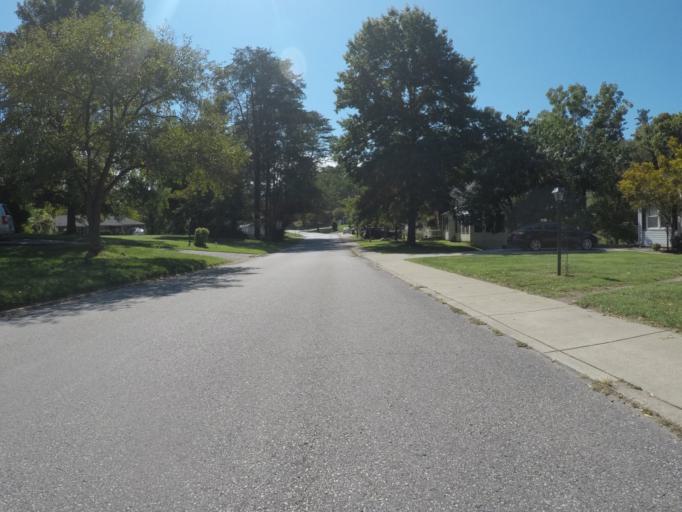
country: US
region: Kentucky
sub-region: Boyd County
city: Ashland
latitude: 38.4489
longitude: -82.6419
